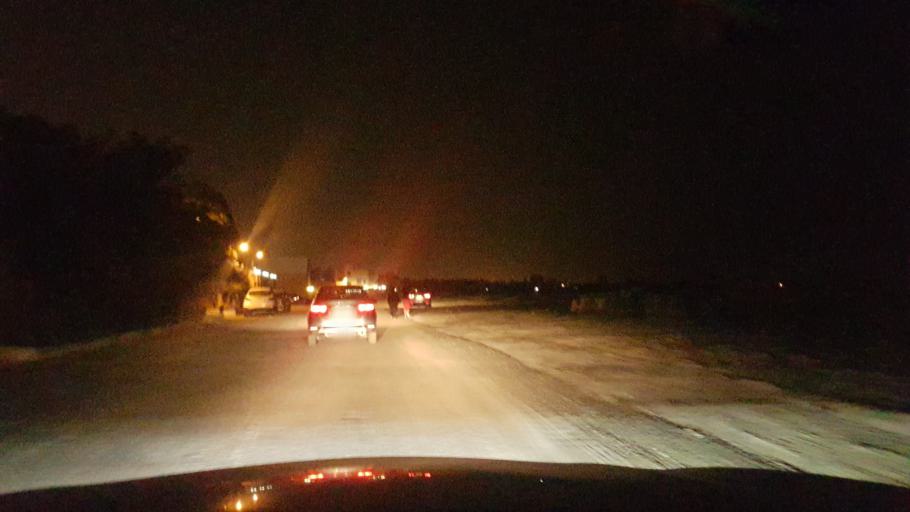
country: BH
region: Central Governorate
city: Madinat Hamad
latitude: 26.0946
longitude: 50.4860
